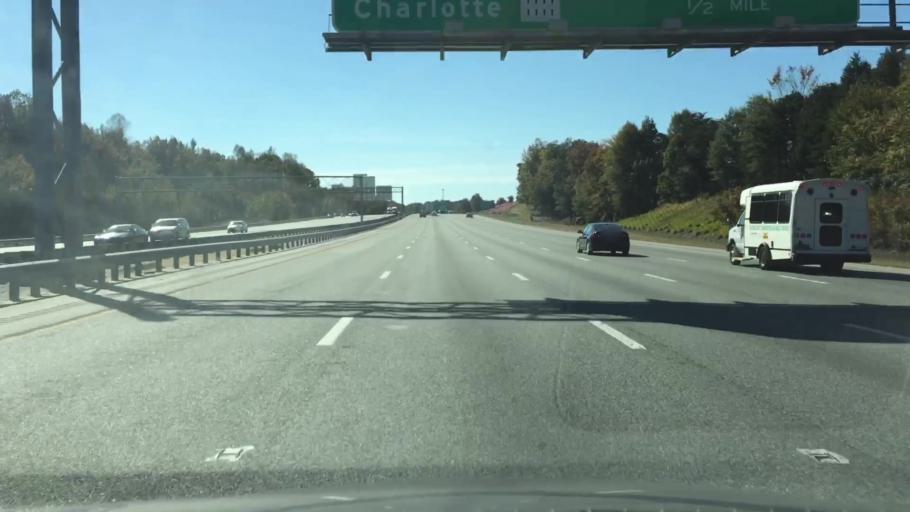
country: US
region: North Carolina
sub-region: Guilford County
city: Jamestown
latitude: 35.9918
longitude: -79.8733
